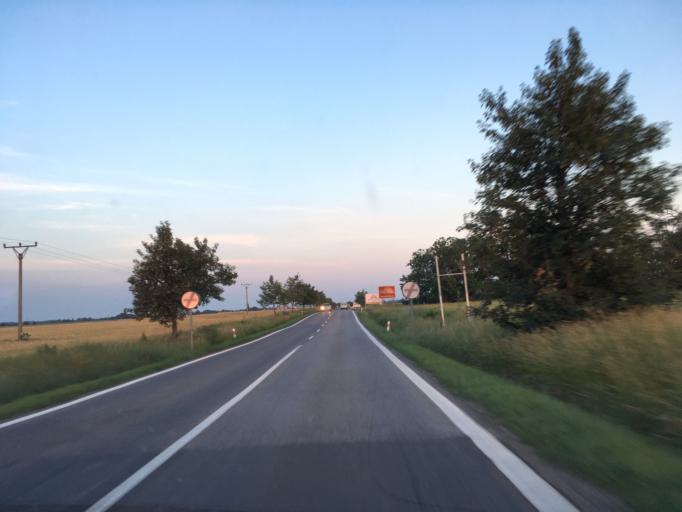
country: SK
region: Nitriansky
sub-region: Okres Nove Zamky
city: Nove Zamky
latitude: 48.0267
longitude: 18.1374
